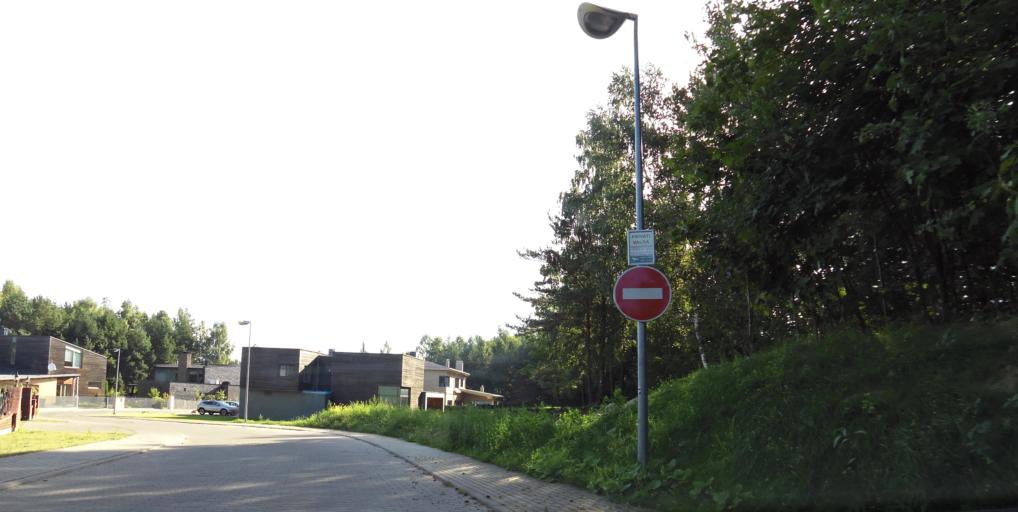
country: LT
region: Vilnius County
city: Seskine
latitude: 54.7037
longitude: 25.2400
